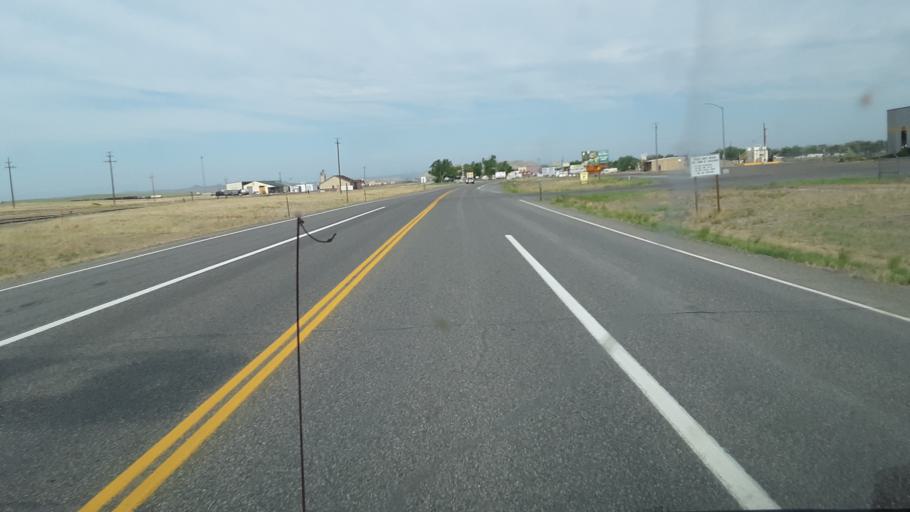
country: US
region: Wyoming
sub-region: Fremont County
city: Riverton
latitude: 43.2359
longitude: -108.0982
